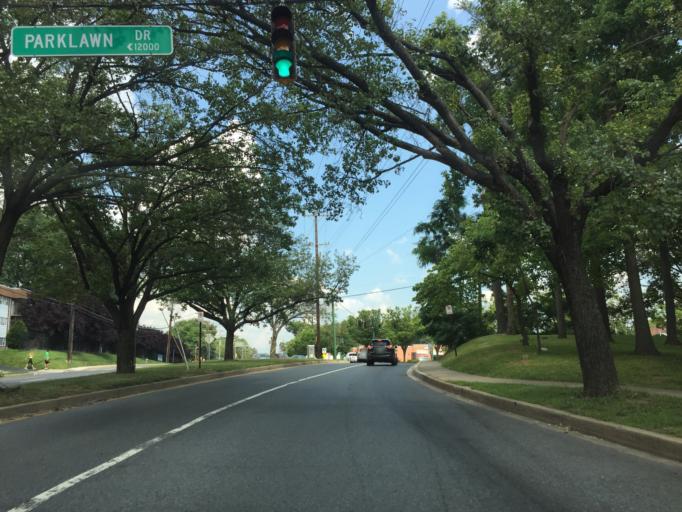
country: US
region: Maryland
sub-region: Montgomery County
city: North Bethesda
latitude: 39.0534
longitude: -77.1067
